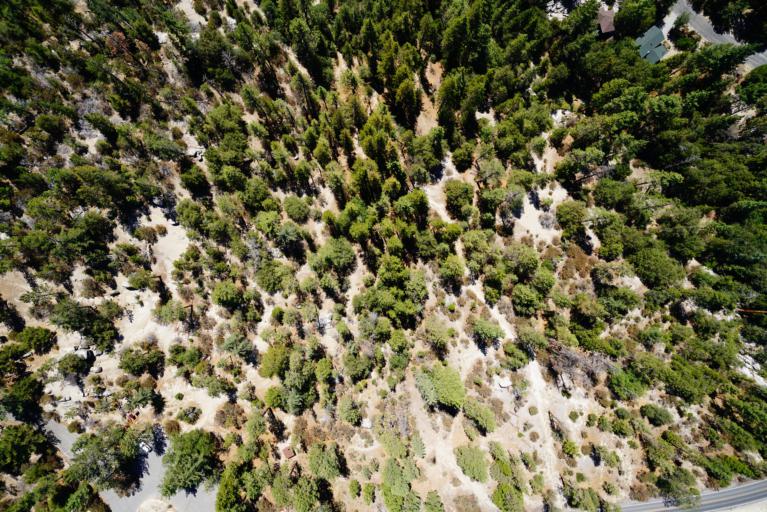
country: US
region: California
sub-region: Riverside County
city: Idyllwild-Pine Cove
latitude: 33.7518
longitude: -116.7230
